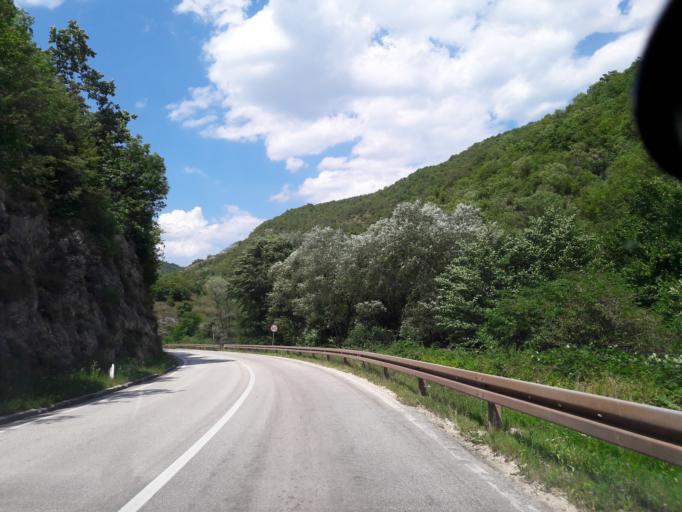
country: BA
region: Republika Srpska
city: Mrkonjic Grad
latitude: 44.4507
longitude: 17.1631
